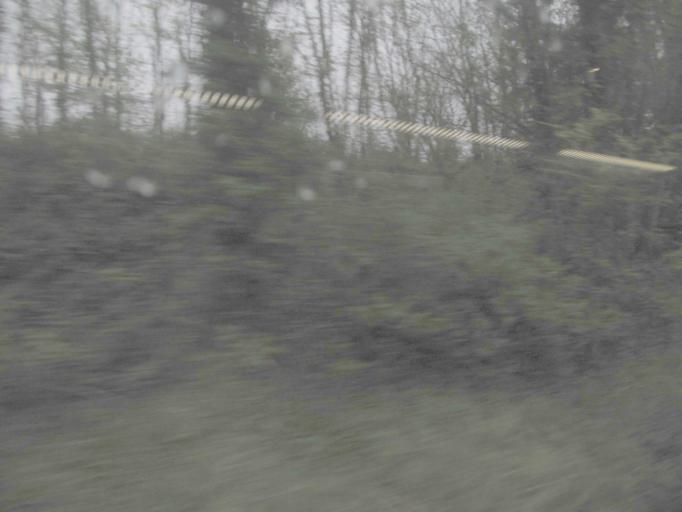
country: GB
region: England
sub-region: Wokingham
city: Earley
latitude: 51.4450
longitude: -0.9278
